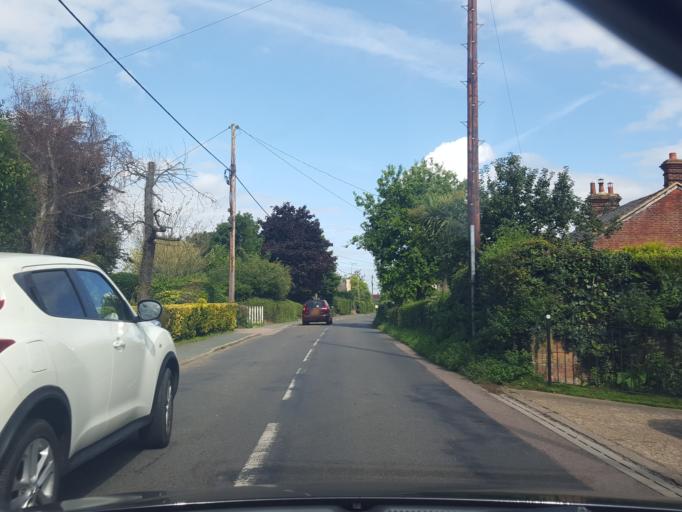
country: GB
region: England
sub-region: Essex
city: Mistley
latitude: 51.9274
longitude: 1.1121
